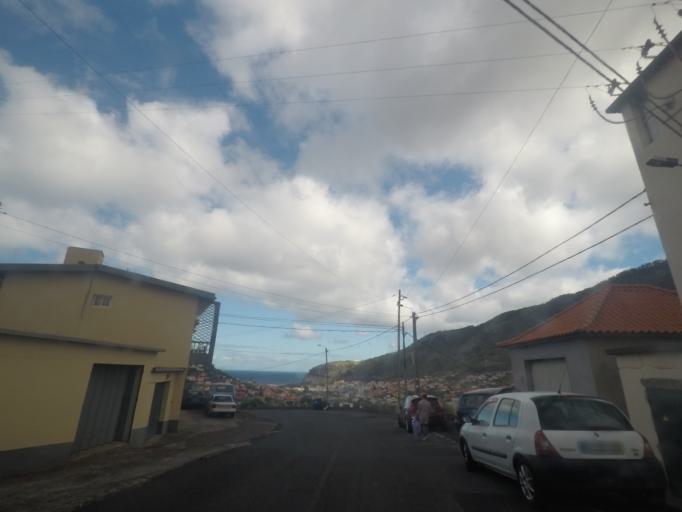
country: PT
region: Madeira
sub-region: Machico
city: Machico
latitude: 32.7310
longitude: -16.7737
